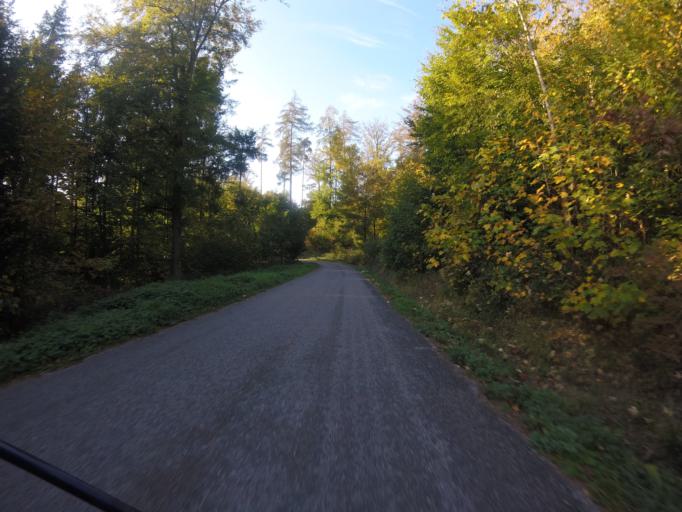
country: DE
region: Baden-Wuerttemberg
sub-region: Regierungsbezirk Stuttgart
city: Oppenweiler
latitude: 48.9838
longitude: 9.4272
